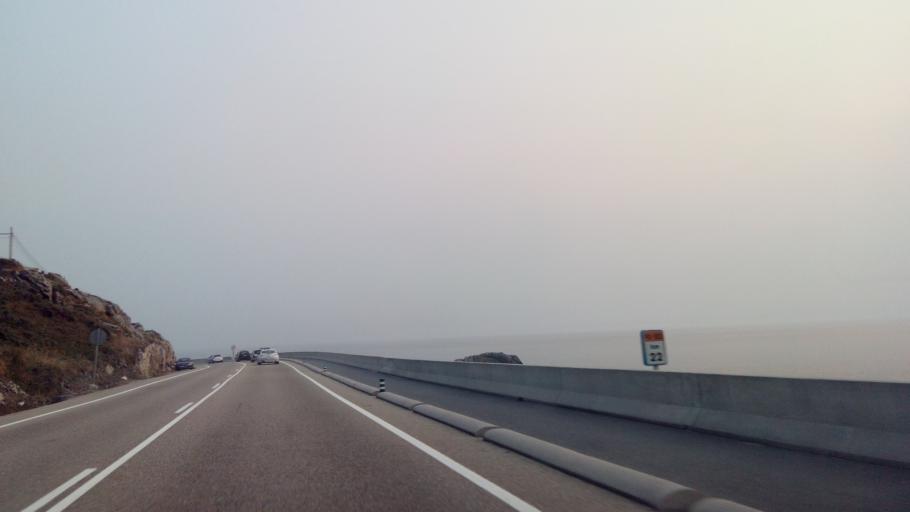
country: ES
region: Galicia
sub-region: Provincia de Pontevedra
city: Baiona
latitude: 42.1052
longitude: -8.8977
